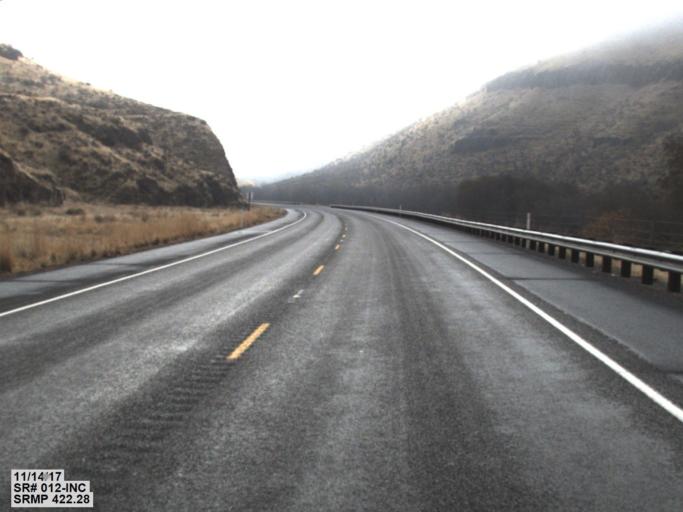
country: US
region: Washington
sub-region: Asotin County
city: Clarkston Heights-Vineland
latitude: 46.4087
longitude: -117.2647
